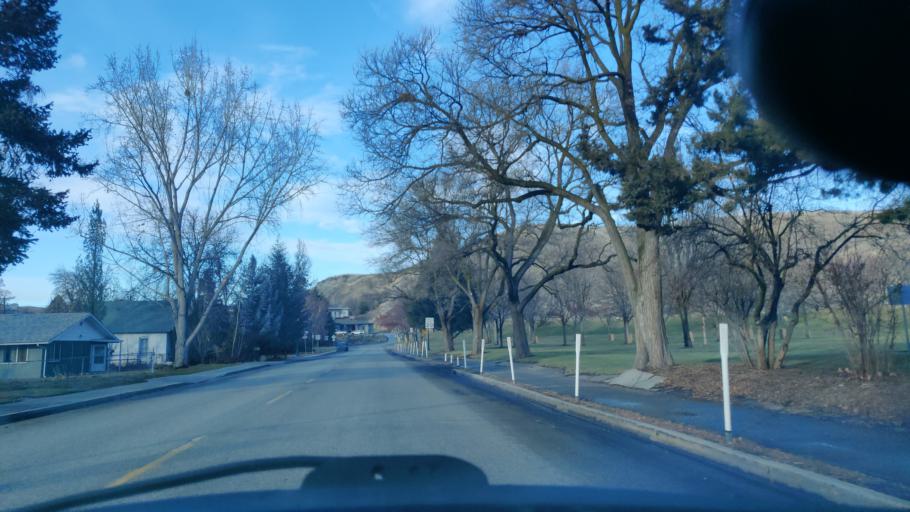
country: US
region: Idaho
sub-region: Ada County
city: Boise
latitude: 43.6347
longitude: -116.2033
